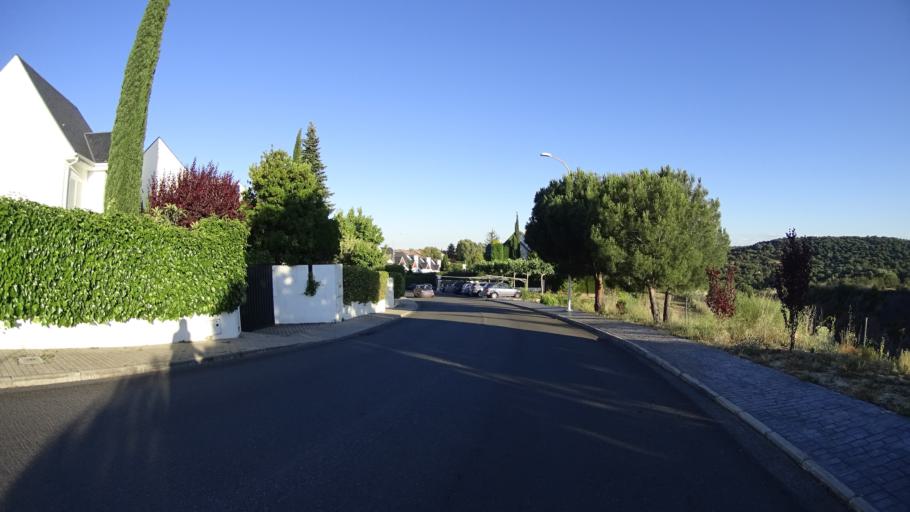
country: ES
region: Madrid
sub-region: Provincia de Madrid
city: Galapagar
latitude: 40.5947
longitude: -3.9732
